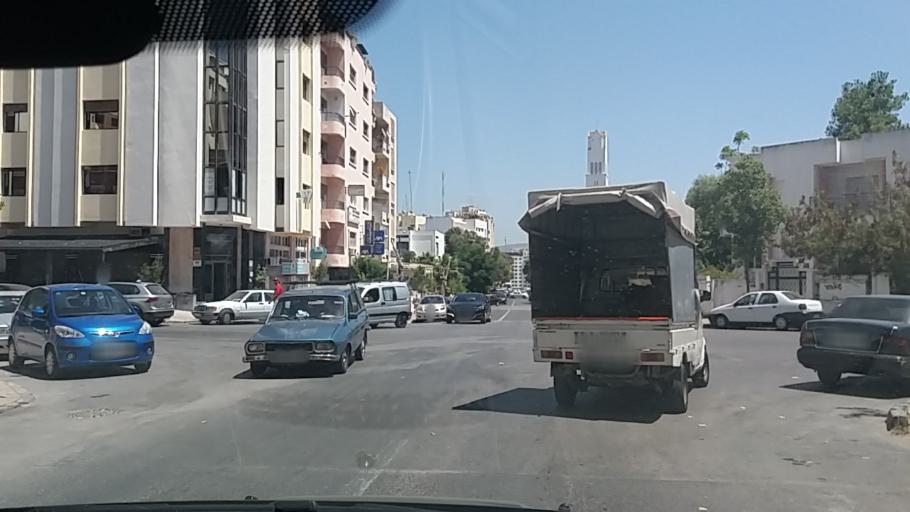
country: MA
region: Tanger-Tetouan
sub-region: Tanger-Assilah
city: Tangier
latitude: 35.7752
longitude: -5.8090
